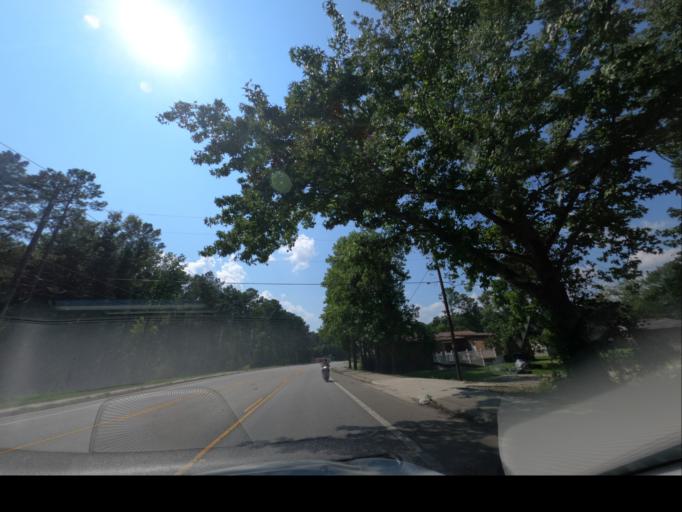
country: US
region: South Carolina
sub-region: Richland County
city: Forest Acres
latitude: 33.9354
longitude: -80.9756
